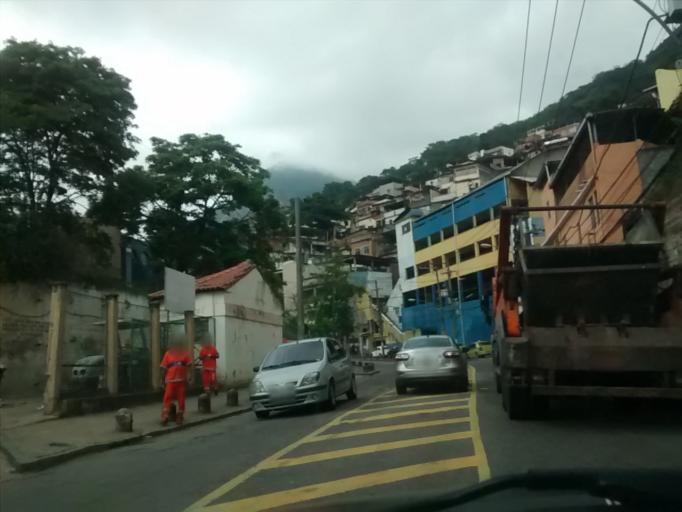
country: BR
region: Rio de Janeiro
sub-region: Rio De Janeiro
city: Rio de Janeiro
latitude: -22.9398
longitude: -43.2528
